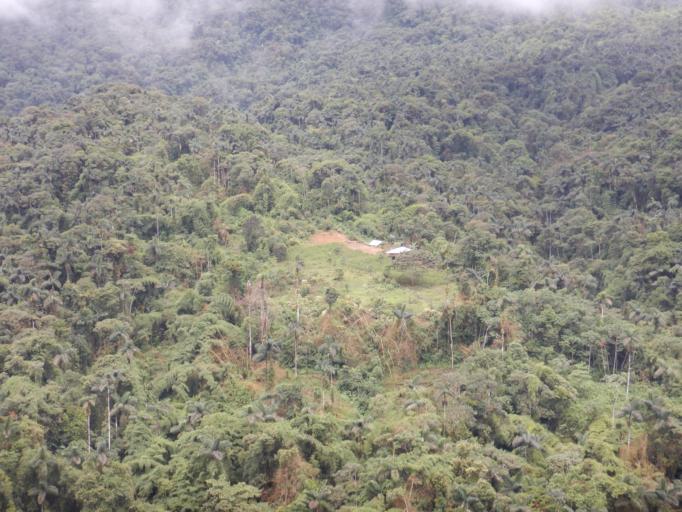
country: BO
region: Cochabamba
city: Totora
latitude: -17.3560
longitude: -65.2106
